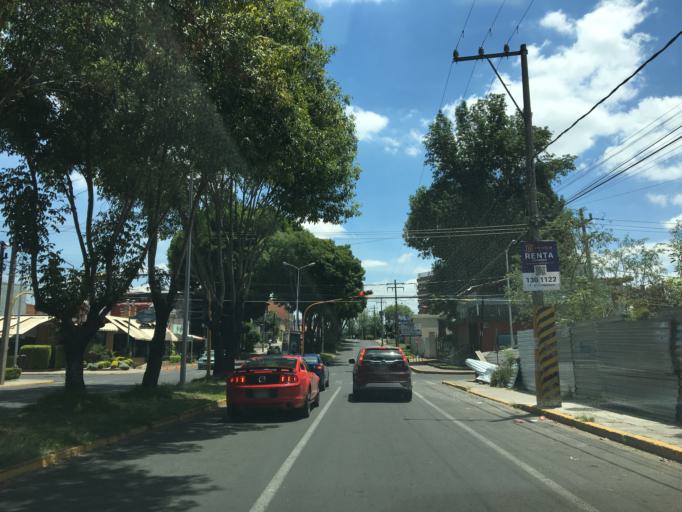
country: MX
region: Puebla
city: Puebla
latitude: 19.0535
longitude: -98.2202
